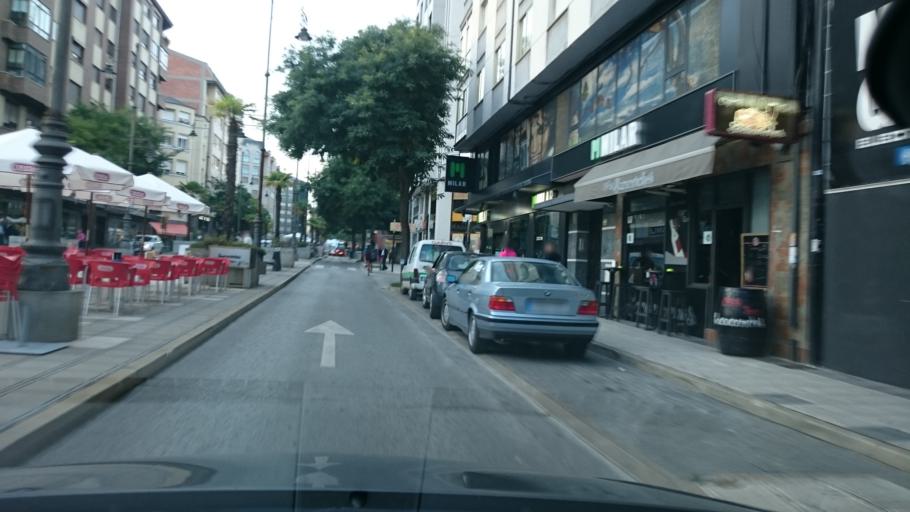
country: ES
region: Castille and Leon
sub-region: Provincia de Leon
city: Ponferrada
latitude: 42.5459
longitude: -6.5973
